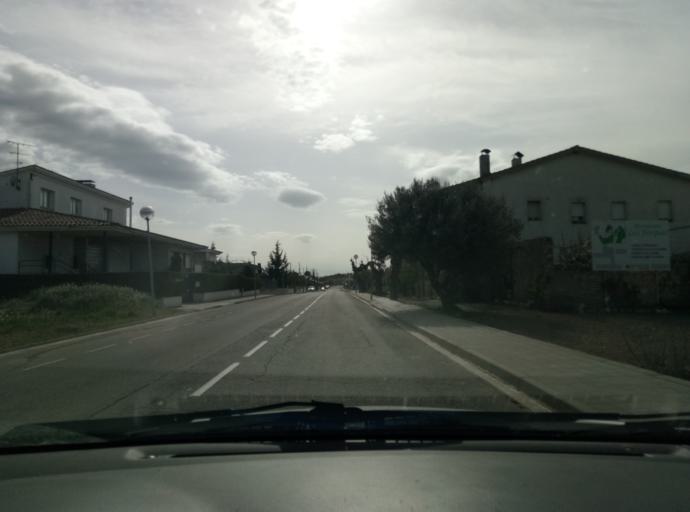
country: ES
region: Catalonia
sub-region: Provincia de Lleida
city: Cervera
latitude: 41.6766
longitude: 1.2845
